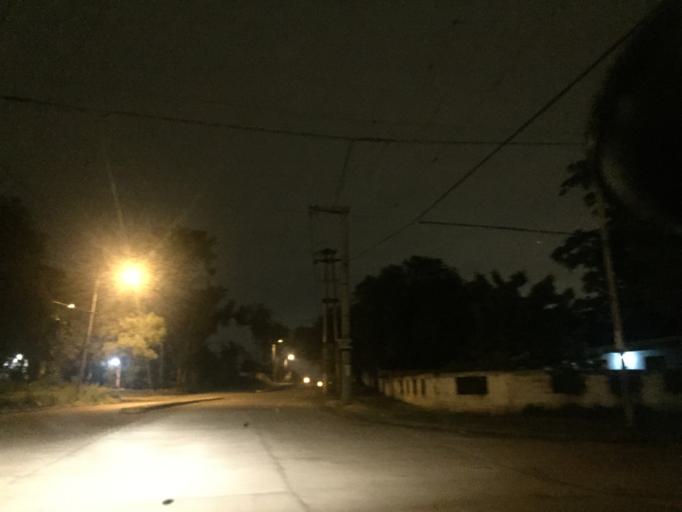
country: AR
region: Cordoba
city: Villa Allende
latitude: -31.3136
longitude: -64.2872
